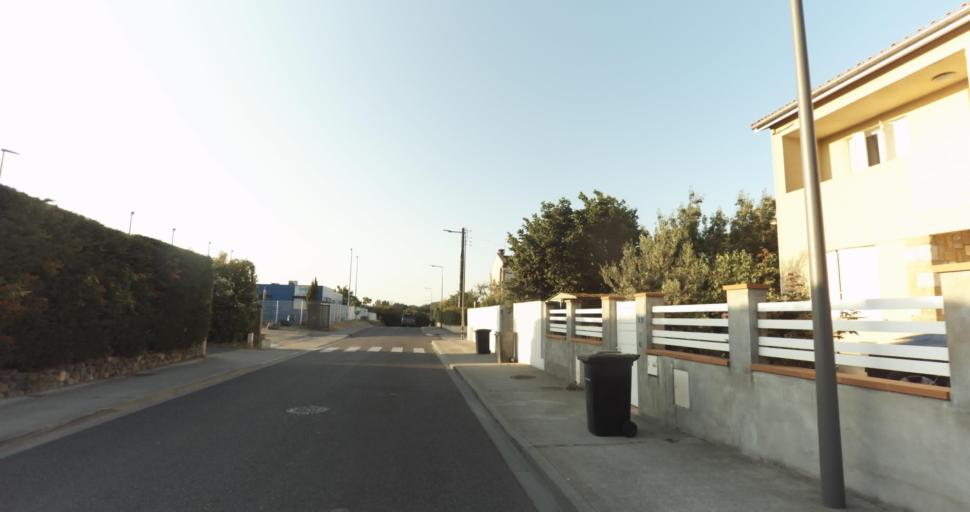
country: FR
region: Midi-Pyrenees
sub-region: Departement de la Haute-Garonne
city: Leguevin
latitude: 43.5979
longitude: 1.2307
